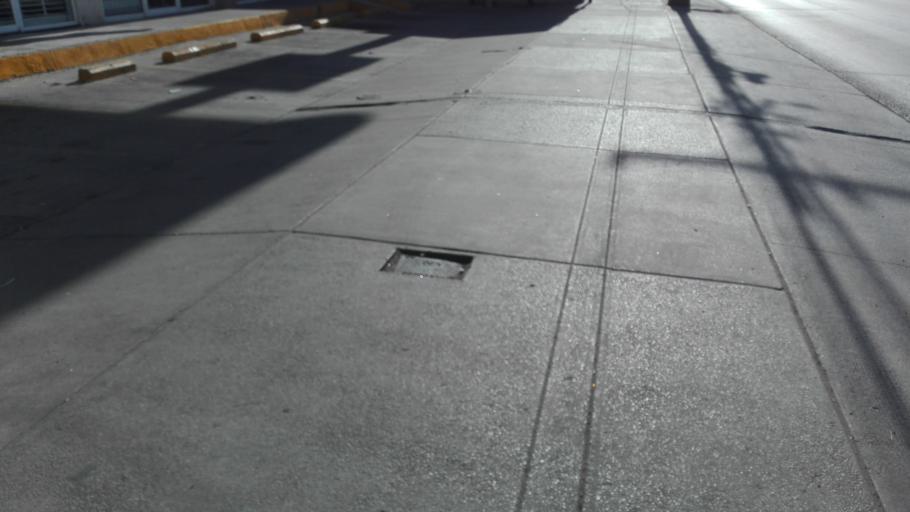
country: MX
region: Chihuahua
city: Ciudad Juarez
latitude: 31.7168
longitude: -106.4136
